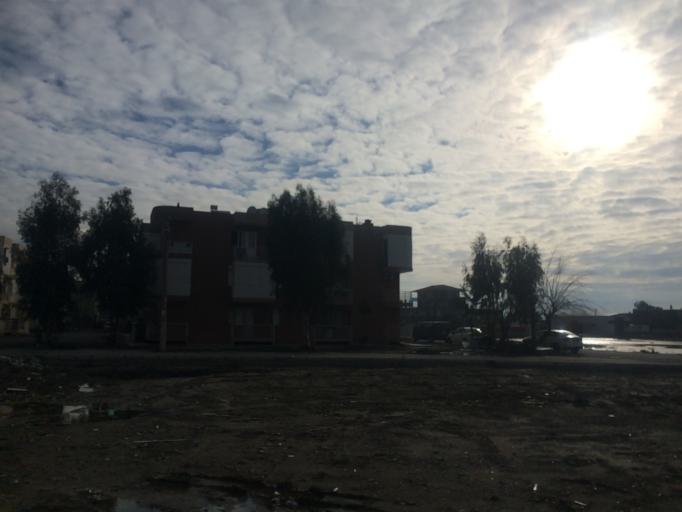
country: TR
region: Izmir
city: Karsiyaka
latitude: 38.4929
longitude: 26.9464
